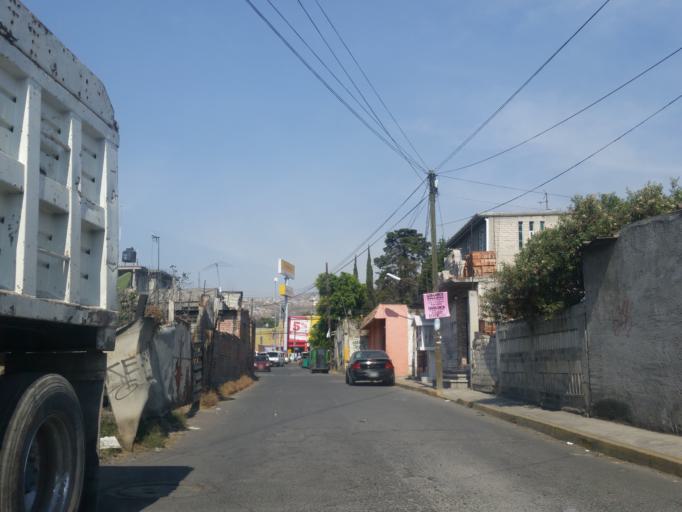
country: MX
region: Mexico
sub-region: La Paz
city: San Isidro
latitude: 19.3263
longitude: -98.9473
